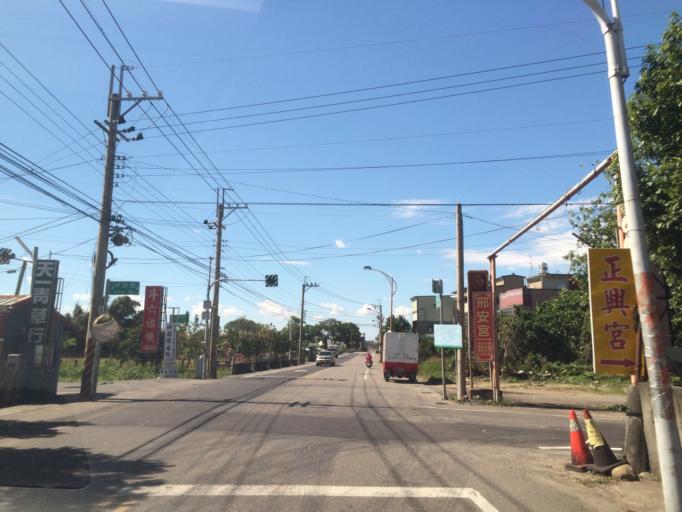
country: TW
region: Taiwan
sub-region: Yunlin
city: Douliu
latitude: 23.7027
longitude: 120.5784
